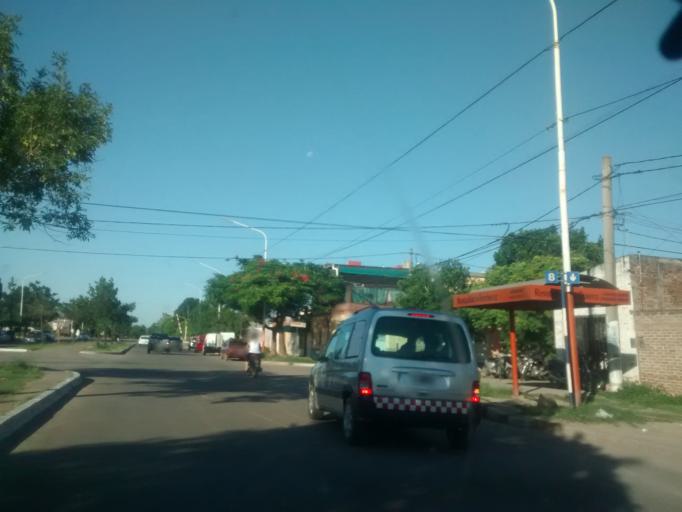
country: AR
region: Chaco
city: Resistencia
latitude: -27.4433
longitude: -59.0063
